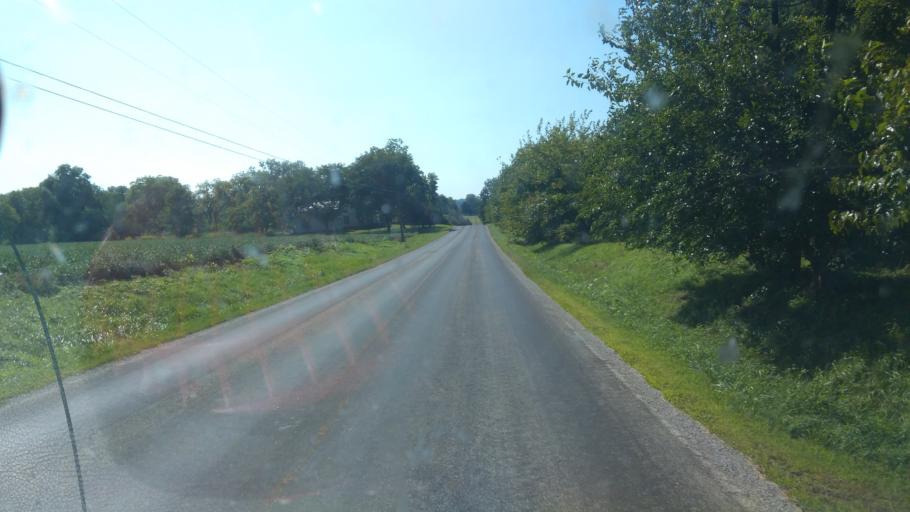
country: US
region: Ohio
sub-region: Ashland County
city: Ashland
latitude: 40.9694
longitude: -82.2964
